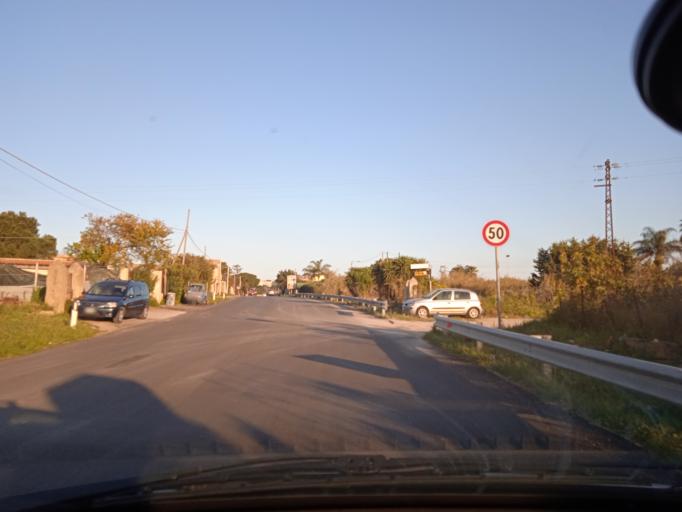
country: IT
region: Sicily
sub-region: Palermo
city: Bagheria
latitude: 38.0901
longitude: 13.4897
